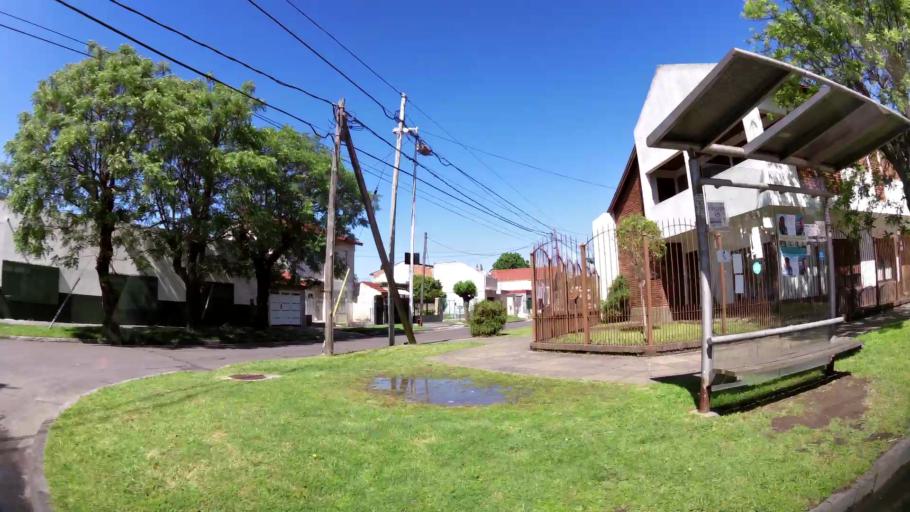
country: AR
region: Buenos Aires
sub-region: Partido de Quilmes
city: Quilmes
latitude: -34.6964
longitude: -58.3024
